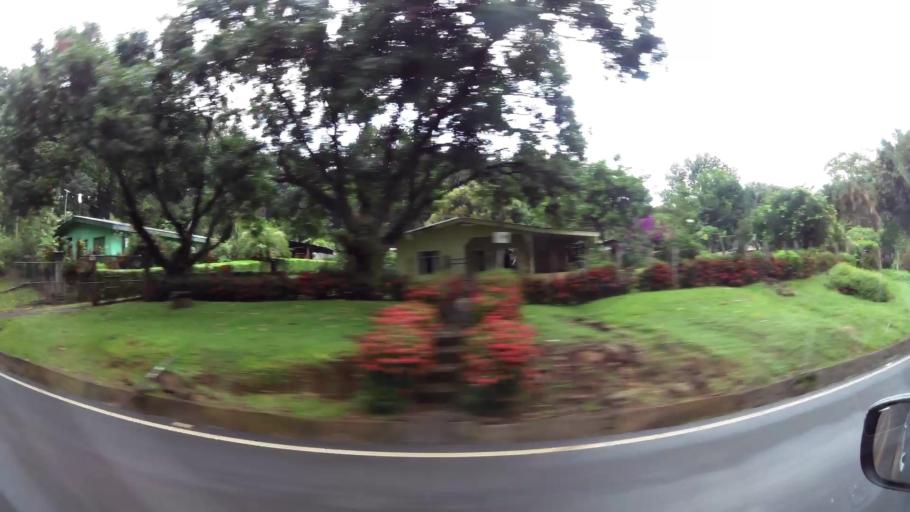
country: CR
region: Alajuela
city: Orotina
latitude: 9.9565
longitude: -84.5748
